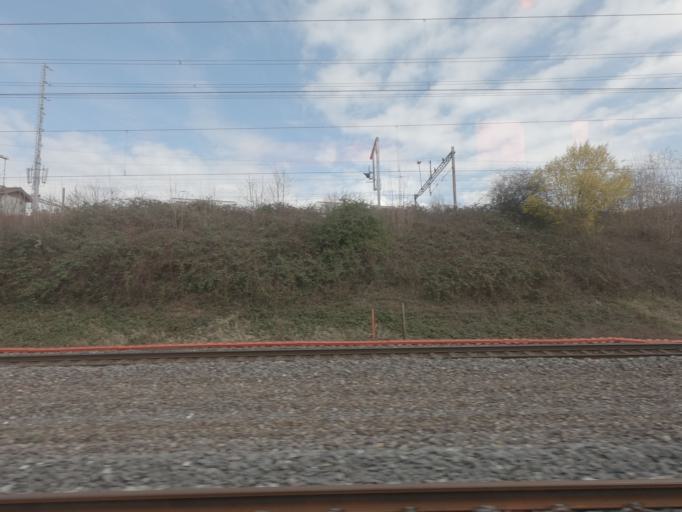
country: CH
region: Vaud
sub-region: Lausanne District
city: Blecherette
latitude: 46.5232
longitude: 6.6124
